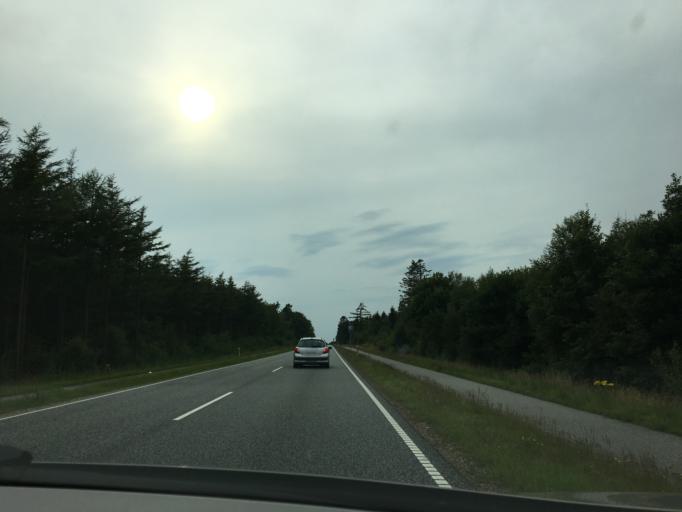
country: DK
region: Central Jutland
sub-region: Ringkobing-Skjern Kommune
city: Ringkobing
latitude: 56.0825
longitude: 8.3446
